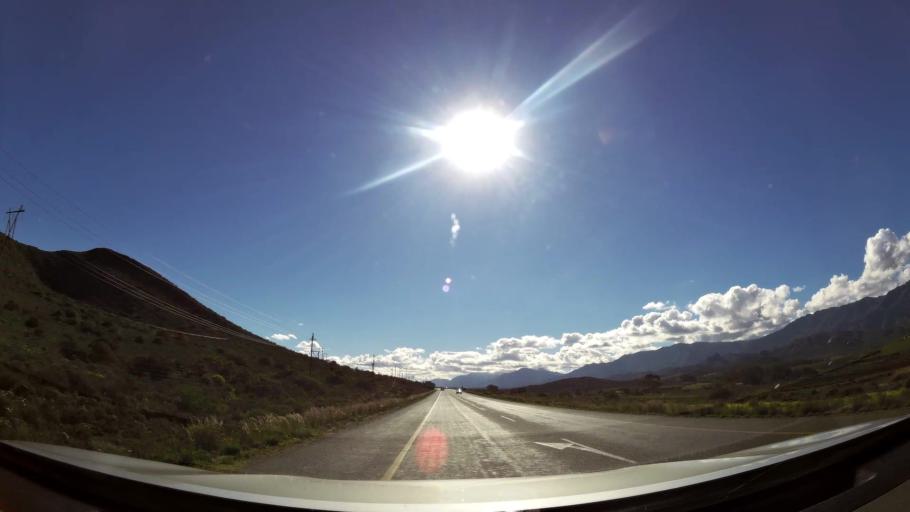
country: ZA
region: Western Cape
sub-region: Cape Winelands District Municipality
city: Ashton
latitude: -33.7817
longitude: 19.7676
